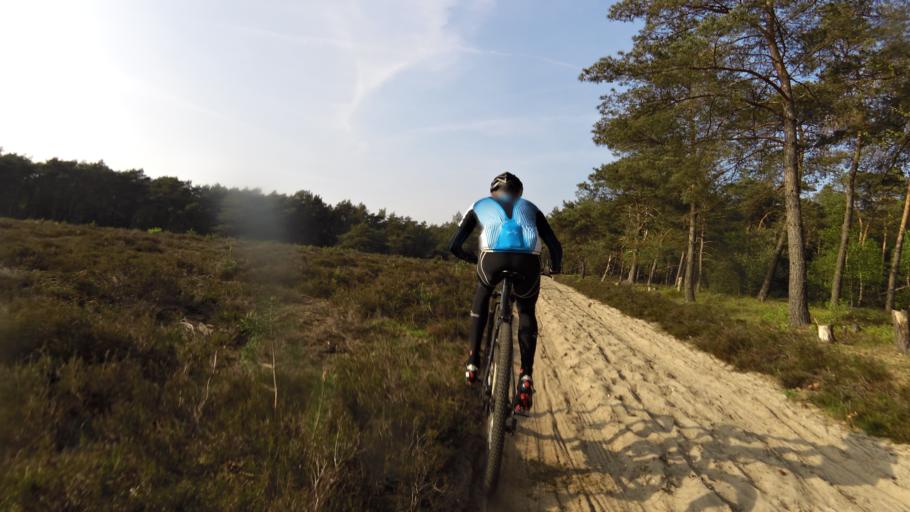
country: NL
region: Gelderland
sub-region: Gemeente Ede
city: Otterlo
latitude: 52.0515
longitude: 5.7417
